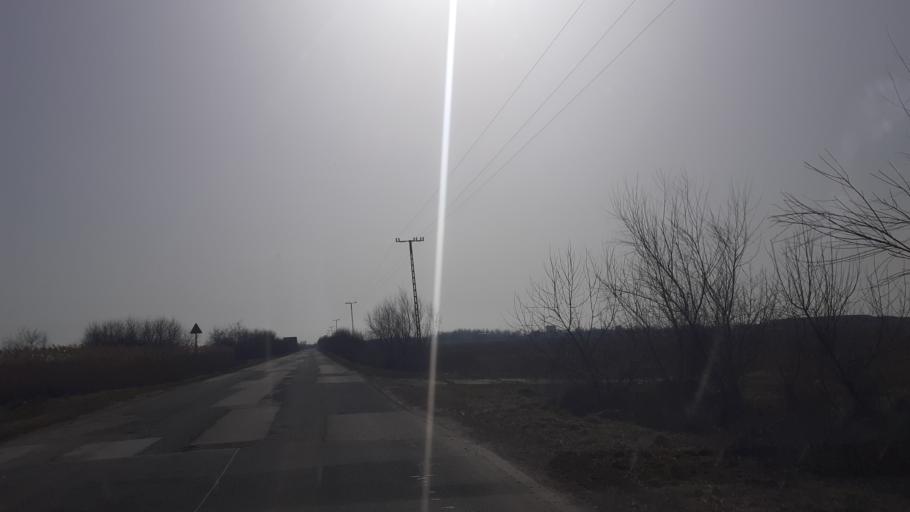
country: HU
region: Pest
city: Bugyi
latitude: 47.2109
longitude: 19.1488
